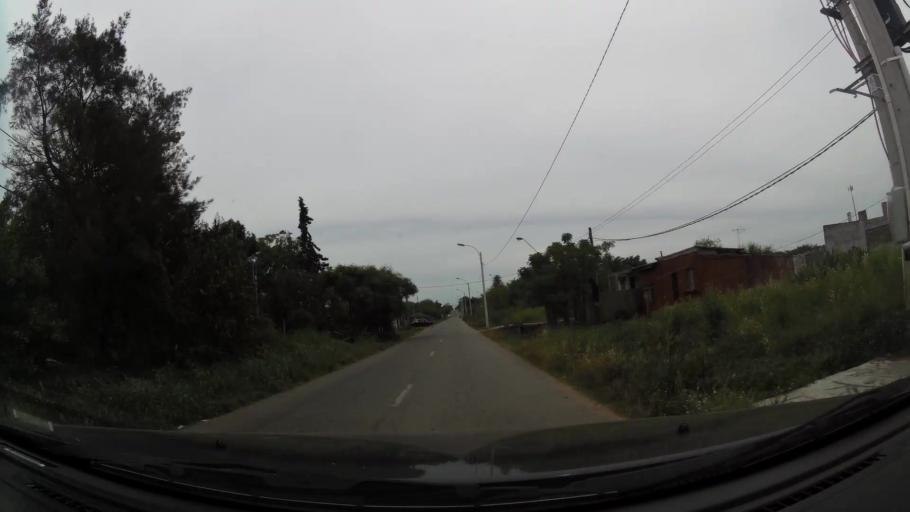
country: UY
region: Canelones
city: Las Piedras
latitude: -34.7418
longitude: -56.2315
